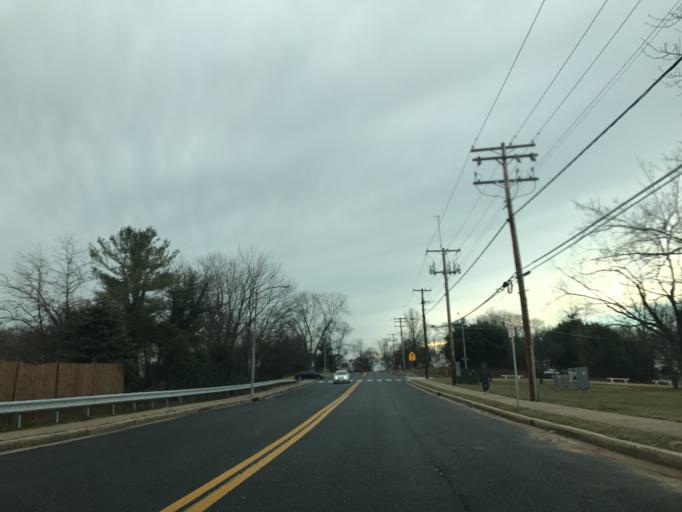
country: US
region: Maryland
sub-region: Baltimore County
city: Carney
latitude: 39.4048
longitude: -76.5272
